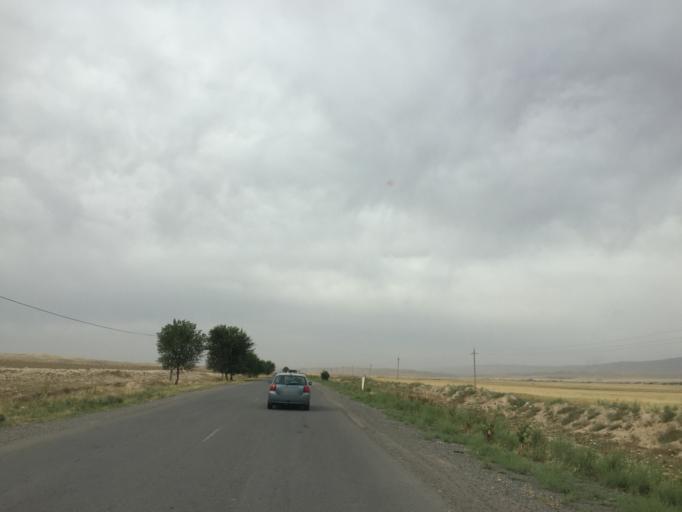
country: TJ
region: Khatlon
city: Danghara
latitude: 37.9897
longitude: 69.3455
